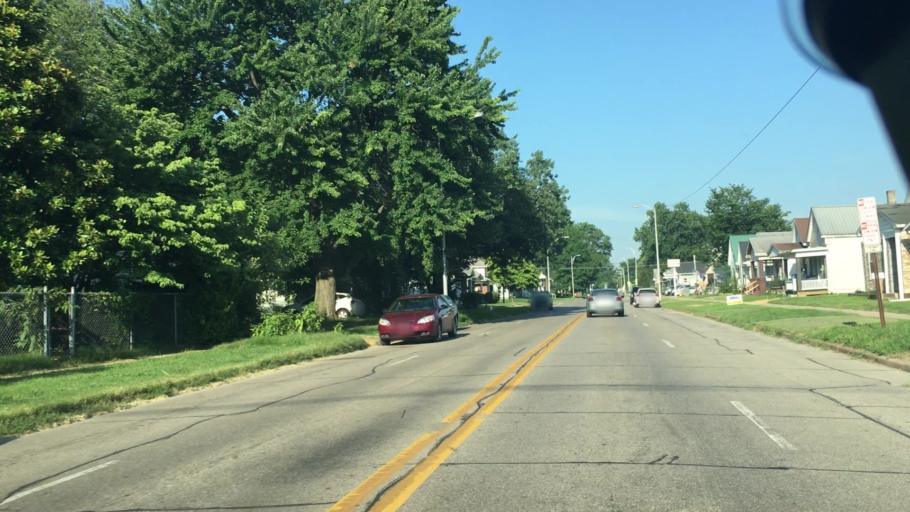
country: US
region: Indiana
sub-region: Vanderburgh County
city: Evansville
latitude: 37.9736
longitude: -87.5409
